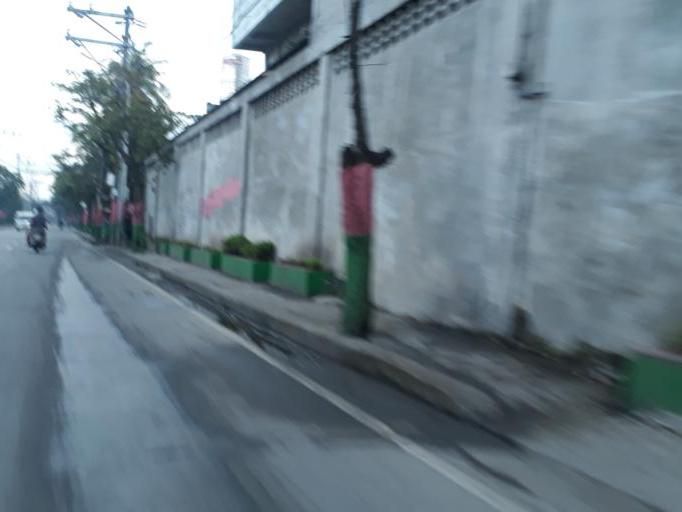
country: PH
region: Calabarzon
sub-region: Province of Rizal
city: Valenzuela
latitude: 14.6932
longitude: 120.9552
